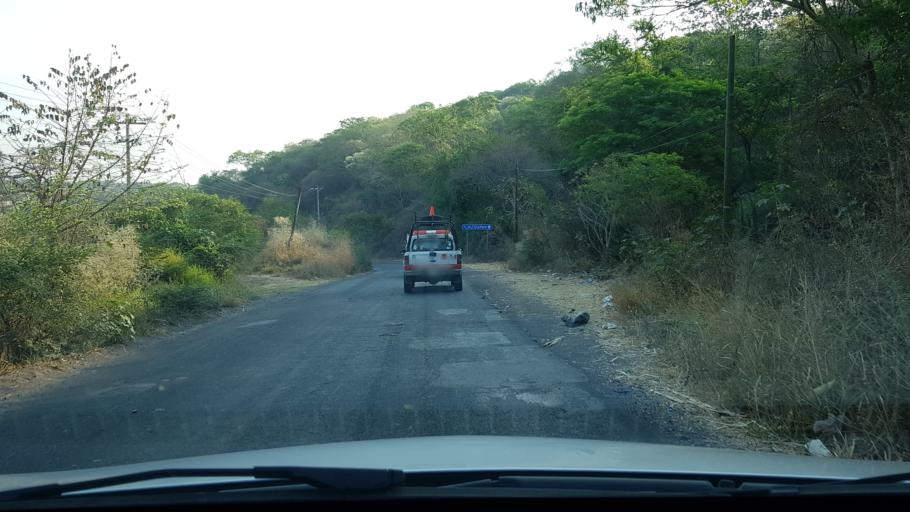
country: MX
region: Morelos
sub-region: Tepalcingo
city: Zacapalco
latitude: 18.6340
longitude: -99.0078
